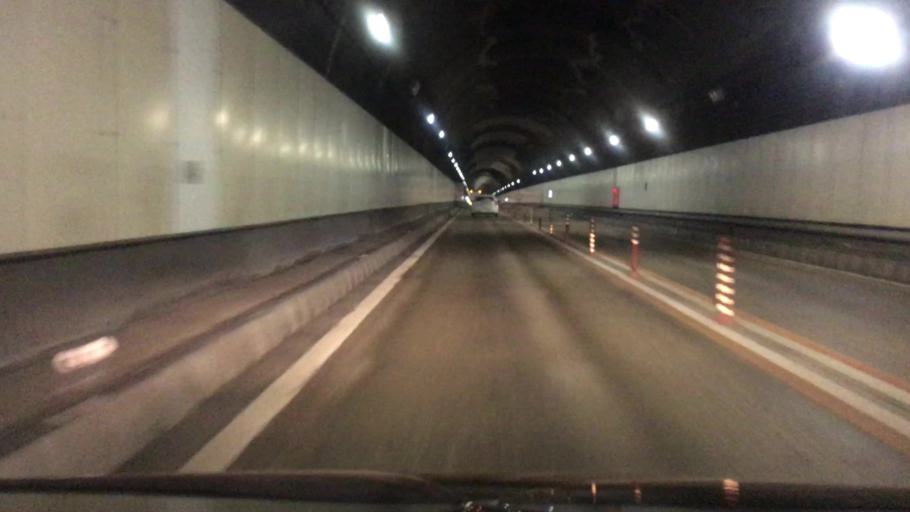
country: JP
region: Kyoto
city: Fukuchiyama
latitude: 35.2995
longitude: 134.9385
